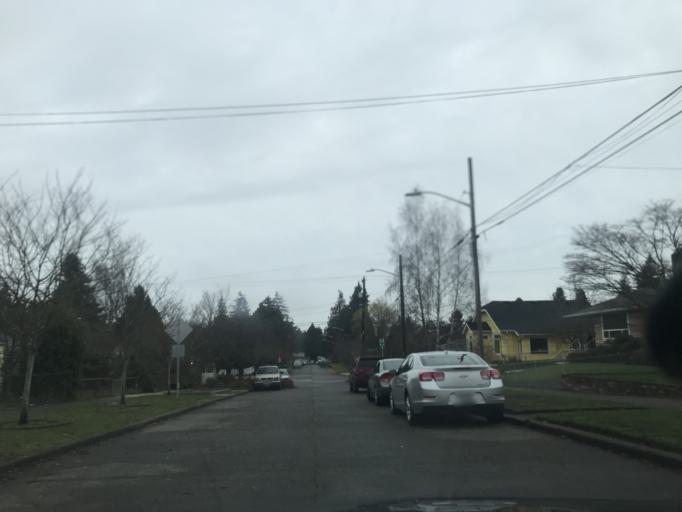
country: US
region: Washington
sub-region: King County
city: White Center
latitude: 47.5312
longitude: -122.3564
